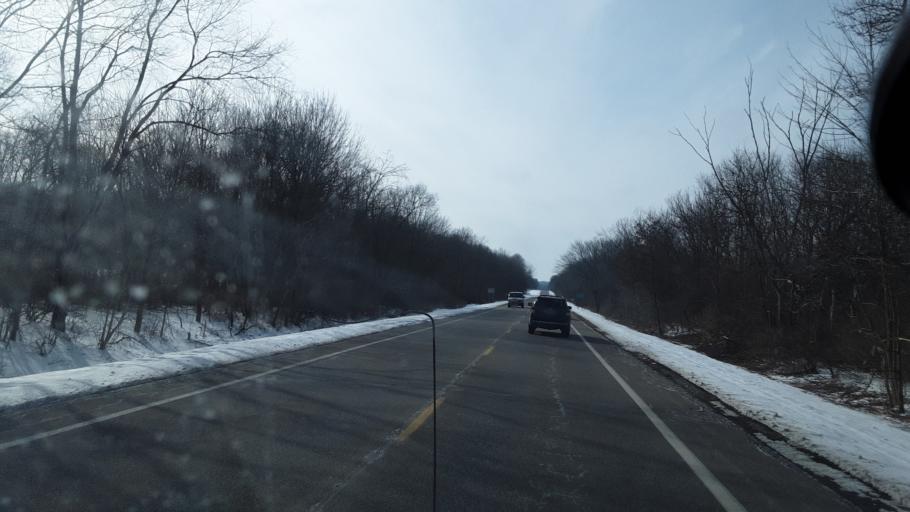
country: US
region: Ohio
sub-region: Stark County
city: Hartville
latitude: 41.0301
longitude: -81.2279
